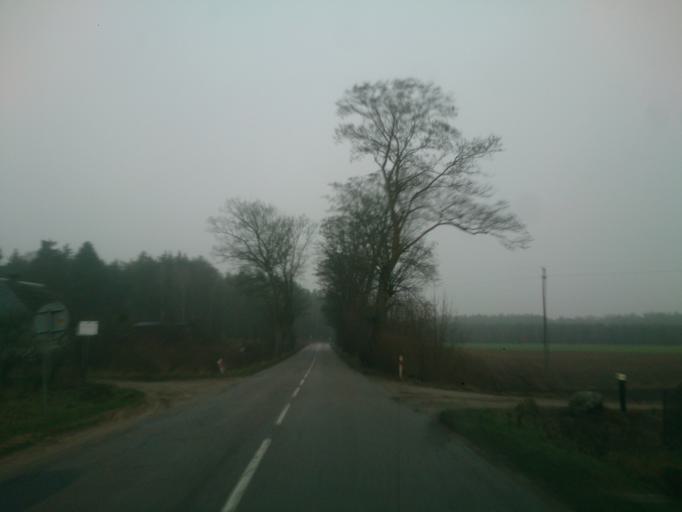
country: PL
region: Pomeranian Voivodeship
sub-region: Powiat starogardzki
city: Lubichowo
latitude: 53.8718
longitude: 18.3810
